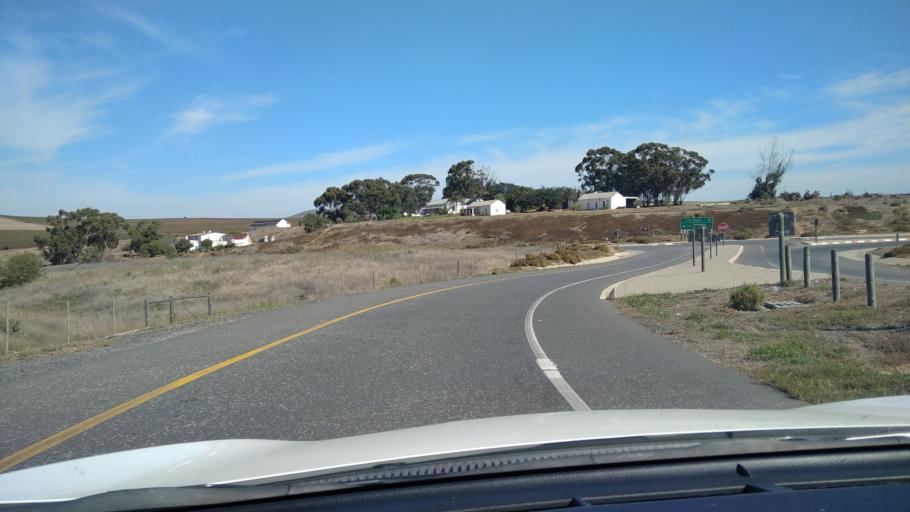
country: ZA
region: Western Cape
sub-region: City of Cape Town
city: Atlantis
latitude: -33.6628
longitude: 18.5616
